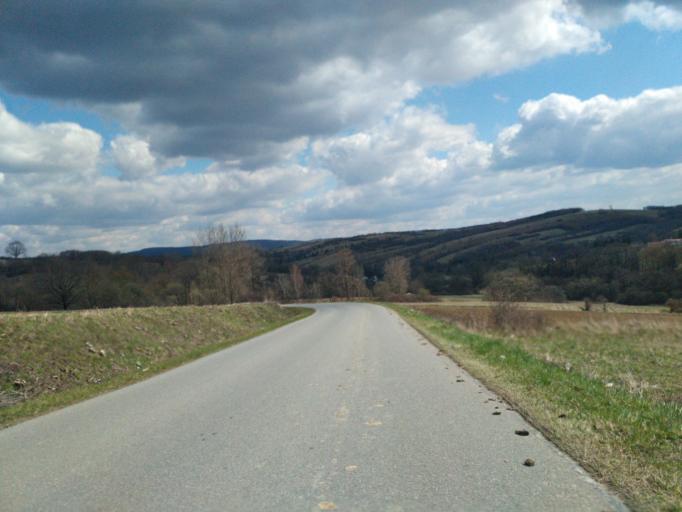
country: PL
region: Subcarpathian Voivodeship
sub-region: Powiat brzozowski
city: Dydnia
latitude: 49.6530
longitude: 22.2144
